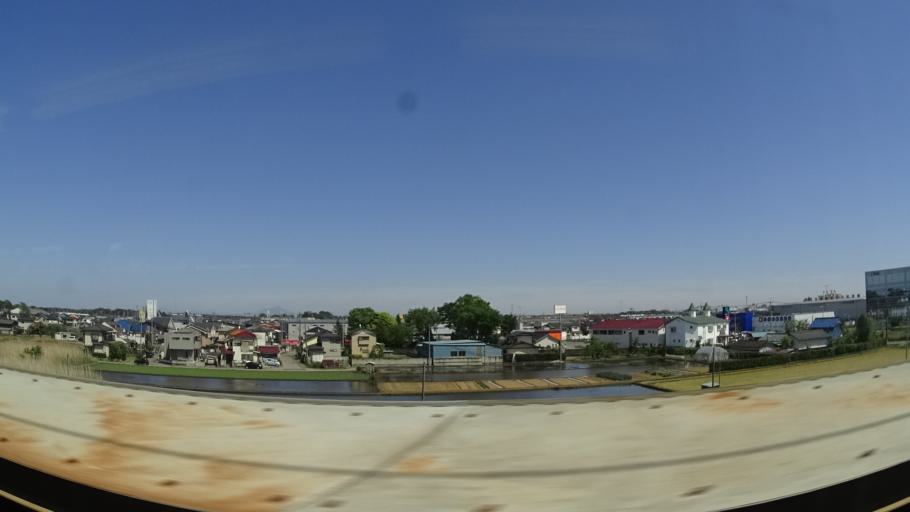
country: JP
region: Ibaraki
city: Koga
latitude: 36.2083
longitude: 139.7504
